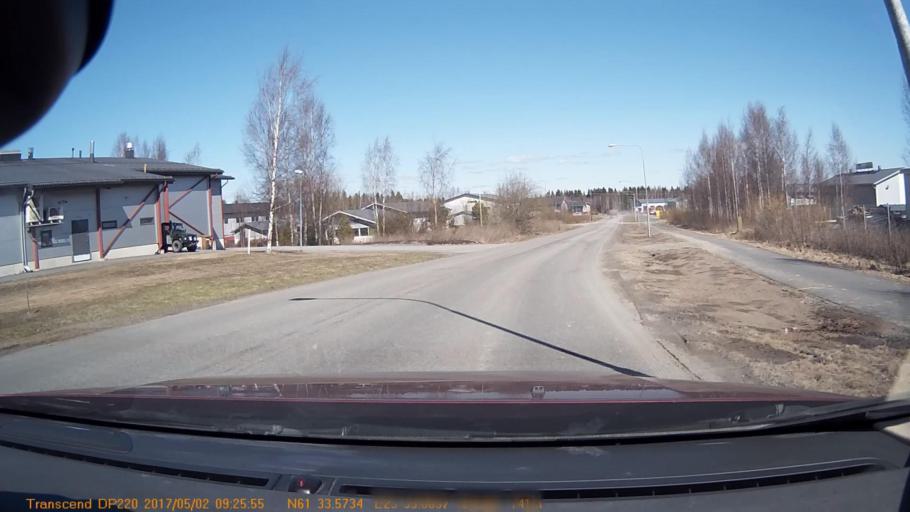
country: FI
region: Pirkanmaa
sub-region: Tampere
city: Yloejaervi
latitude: 61.5596
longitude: 23.5515
